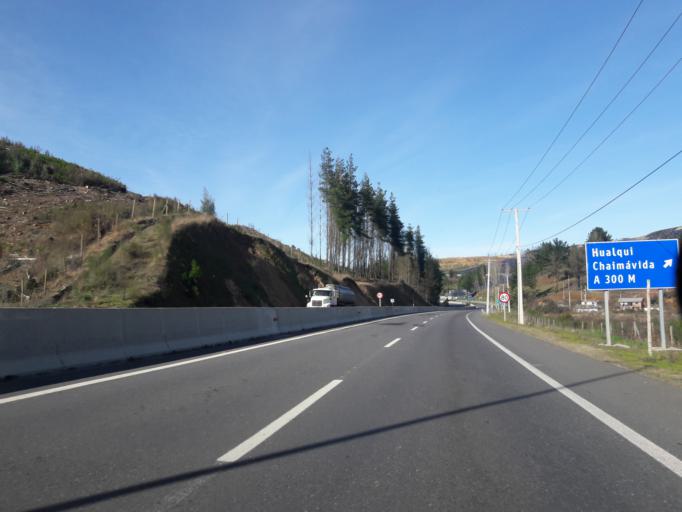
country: CL
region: Biobio
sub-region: Provincia de Concepcion
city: Penco
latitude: -36.8599
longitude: -72.8596
